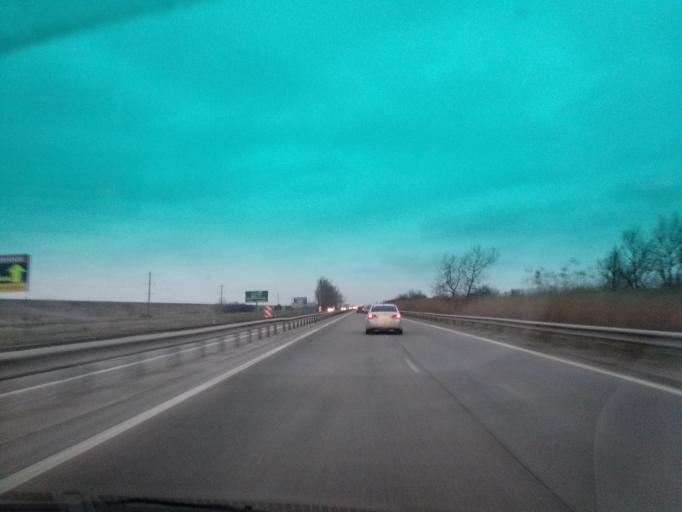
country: RU
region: Adygeya
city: Tlyustenkhabl'
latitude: 44.9396
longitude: 39.1306
